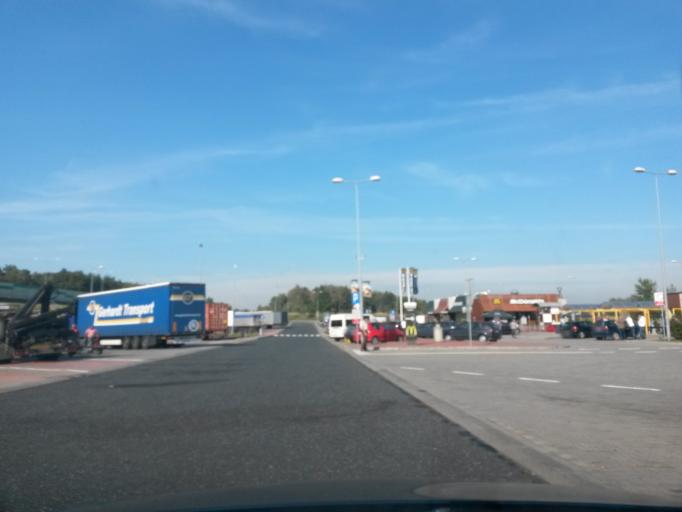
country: PL
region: Silesian Voivodeship
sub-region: Powiat gliwicki
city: Sosnicowice
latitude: 50.3107
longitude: 18.5520
